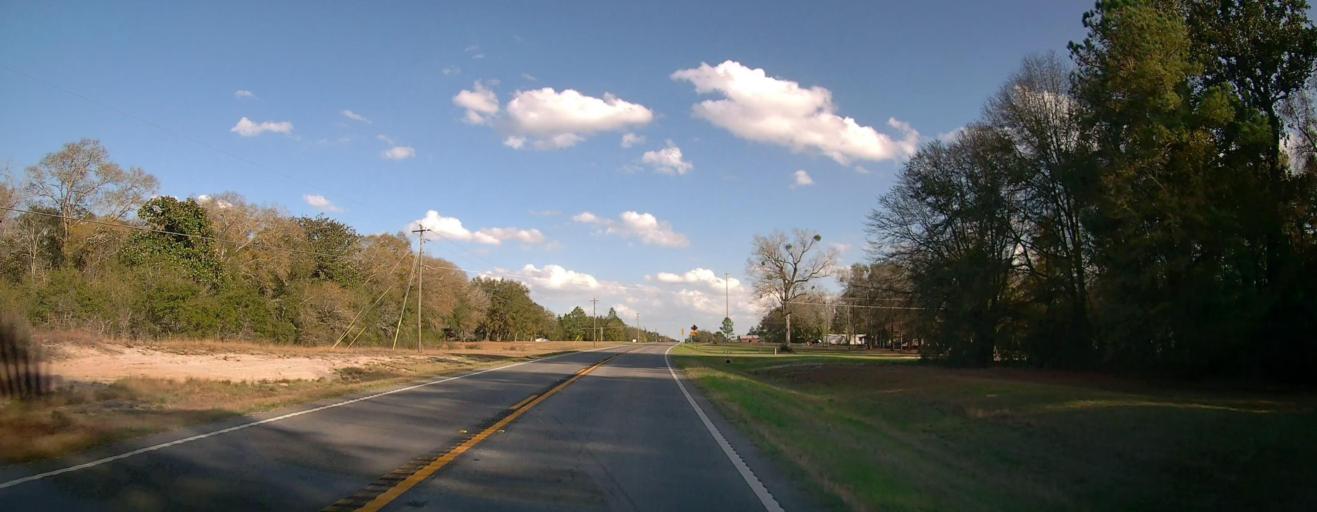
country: US
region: Georgia
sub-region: Tattnall County
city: Reidsville
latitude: 32.1158
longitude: -82.1862
